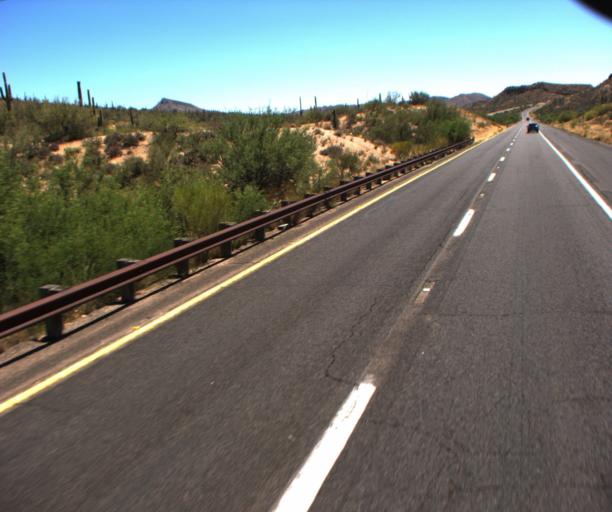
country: US
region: Arizona
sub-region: Maricopa County
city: Rio Verde
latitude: 33.7631
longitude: -111.4953
